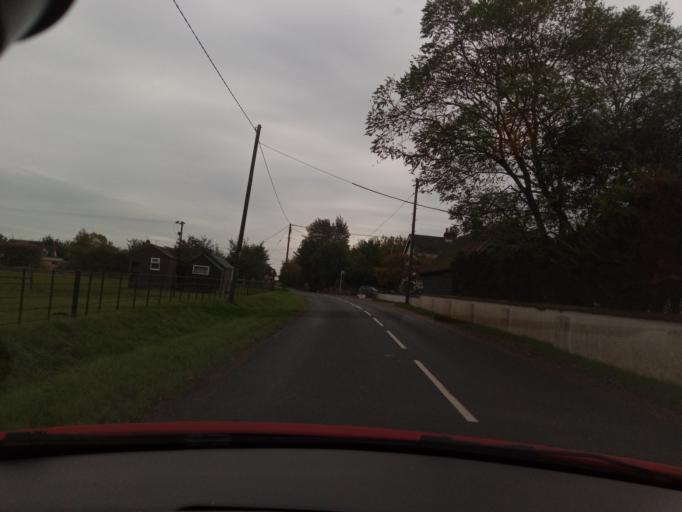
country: GB
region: England
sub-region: Essex
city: West Mersea
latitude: 51.7898
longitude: 0.9365
